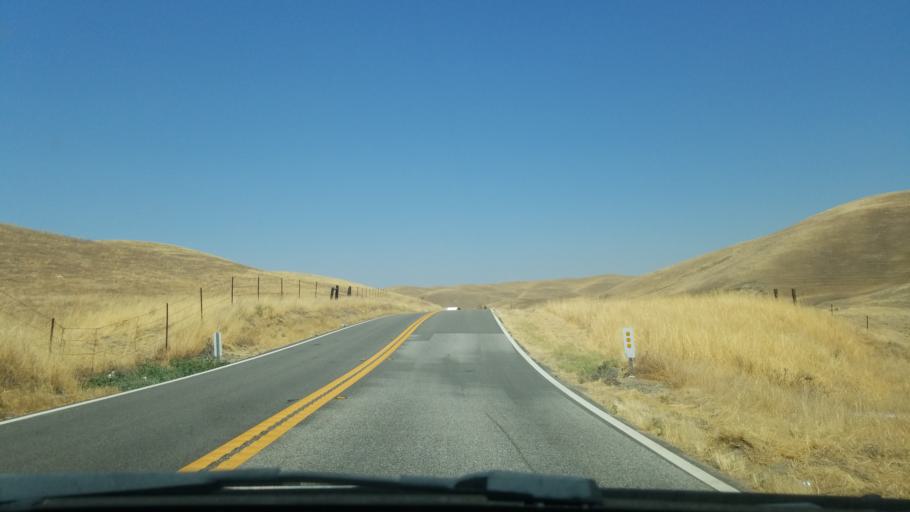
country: US
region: California
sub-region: San Luis Obispo County
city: Shandon
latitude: 35.5792
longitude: -120.4346
